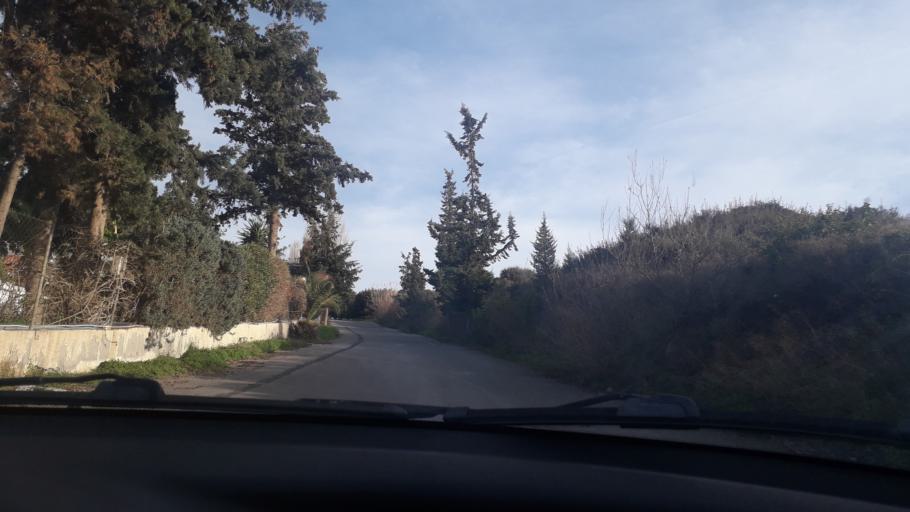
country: GR
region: Crete
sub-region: Nomos Rethymnis
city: Panormos
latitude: 35.3902
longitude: 24.6120
